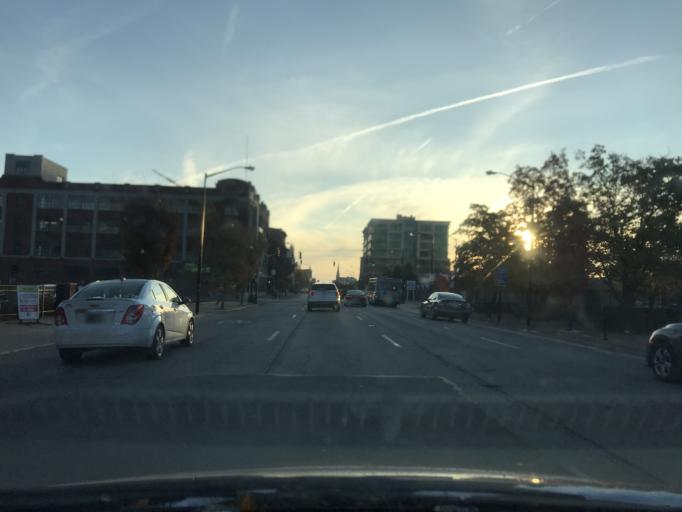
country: US
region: Kentucky
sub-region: Jefferson County
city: Louisville
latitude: 38.2546
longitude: -85.7510
